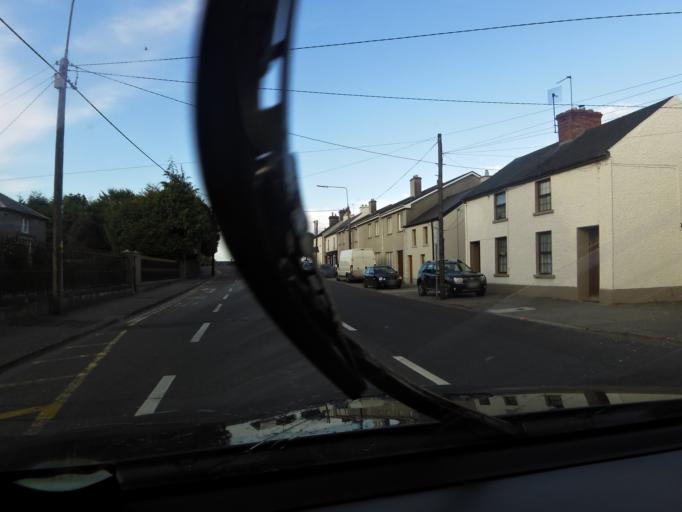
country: IE
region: Connaught
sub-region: County Galway
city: Ballinasloe
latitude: 53.3284
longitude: -8.2300
